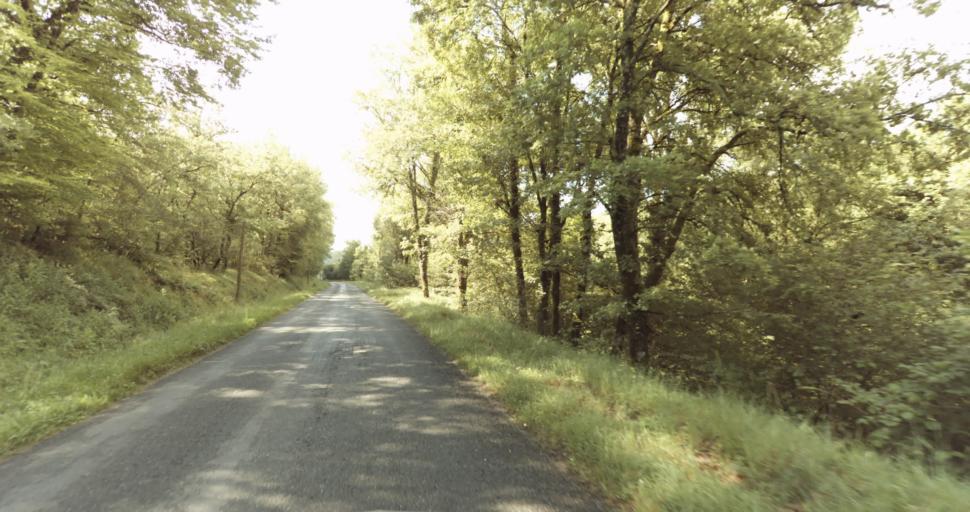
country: FR
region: Aquitaine
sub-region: Departement de la Dordogne
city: Lalinde
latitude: 44.8875
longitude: 0.7731
